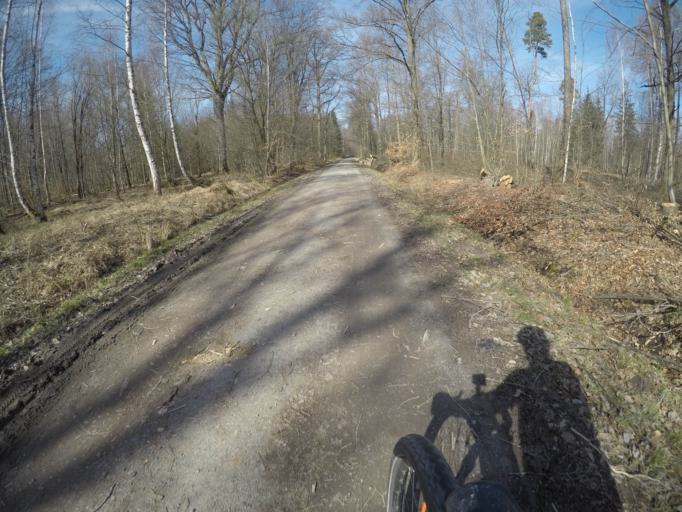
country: DE
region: Baden-Wuerttemberg
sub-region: Regierungsbezirk Stuttgart
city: Gerlingen
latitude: 48.7681
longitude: 9.0751
